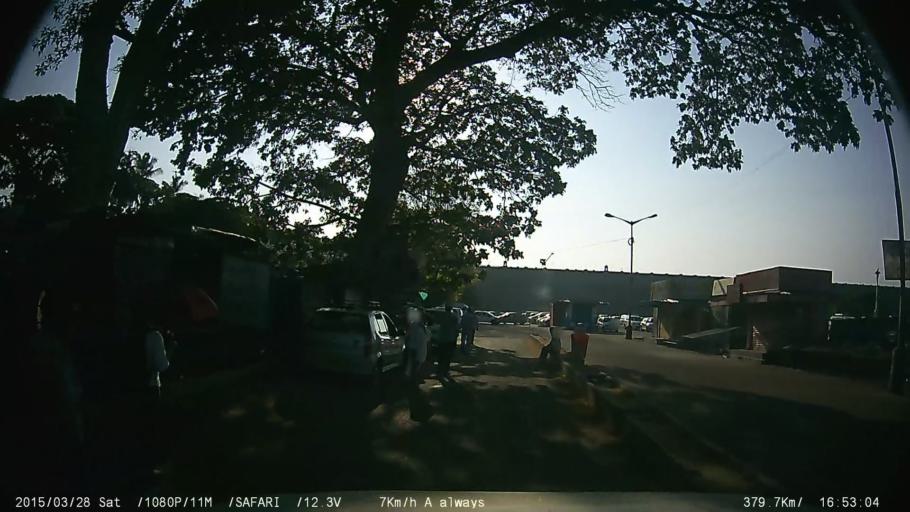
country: IN
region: Karnataka
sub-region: Mandya
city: Shrirangapattana
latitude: 12.4234
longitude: 76.5759
